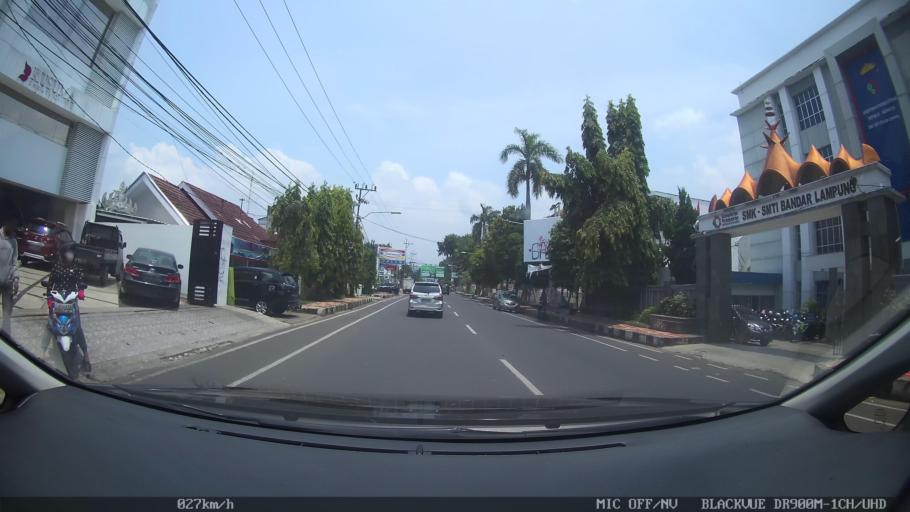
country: ID
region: Lampung
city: Bandarlampung
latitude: -5.4227
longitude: 105.2664
